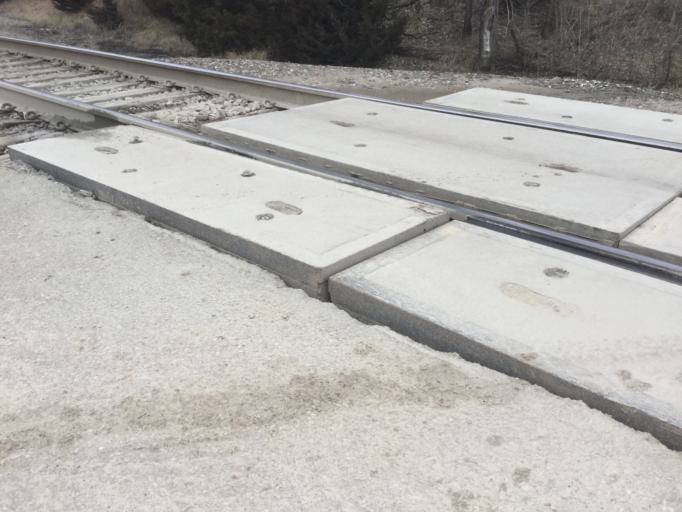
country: US
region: Kansas
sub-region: Butler County
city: Rose Hill
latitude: 37.5351
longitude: -97.1713
